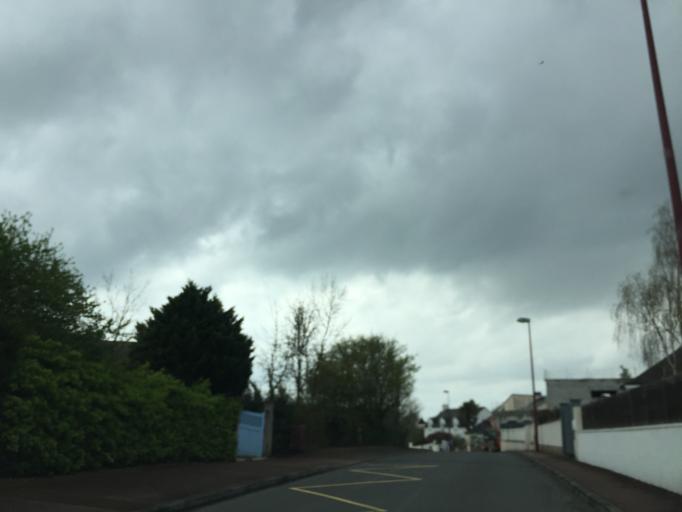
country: FR
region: Pays de la Loire
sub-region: Departement de la Loire-Atlantique
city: Suce-sur-Erdre
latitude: 47.3371
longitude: -1.5161
